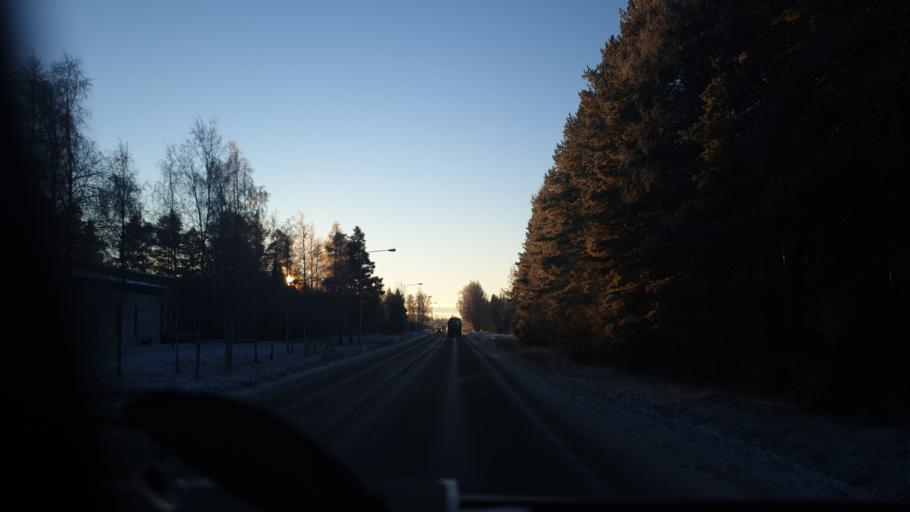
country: FI
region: Northern Ostrobothnia
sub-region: Ylivieska
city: Kalajoki
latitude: 64.2711
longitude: 23.9490
